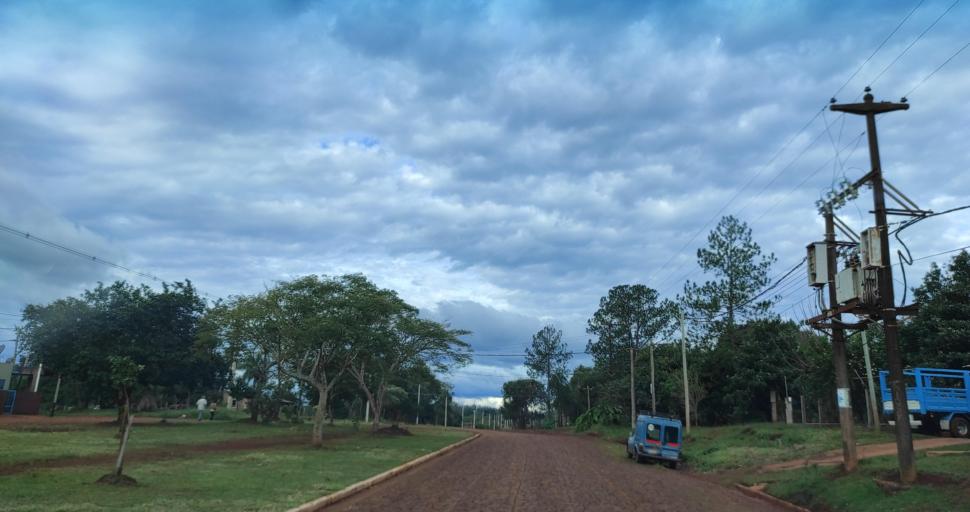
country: AR
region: Misiones
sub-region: Departamento de Candelaria
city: Candelaria
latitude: -27.4630
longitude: -55.7321
